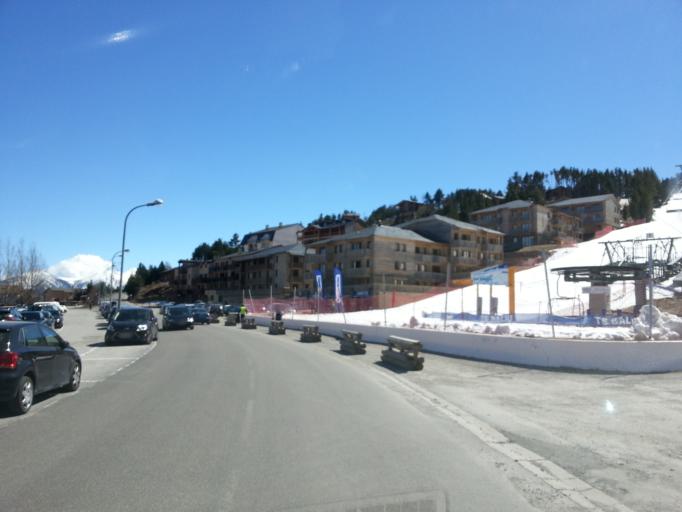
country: ES
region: Catalonia
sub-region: Provincia de Girona
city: Llivia
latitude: 42.5734
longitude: 2.0705
